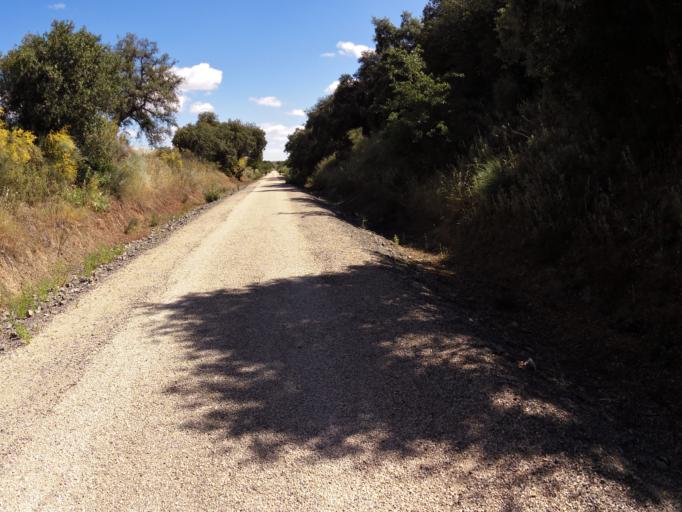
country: ES
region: Andalusia
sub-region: Provincia de Jaen
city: Alcaudete
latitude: 37.6258
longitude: -4.0913
